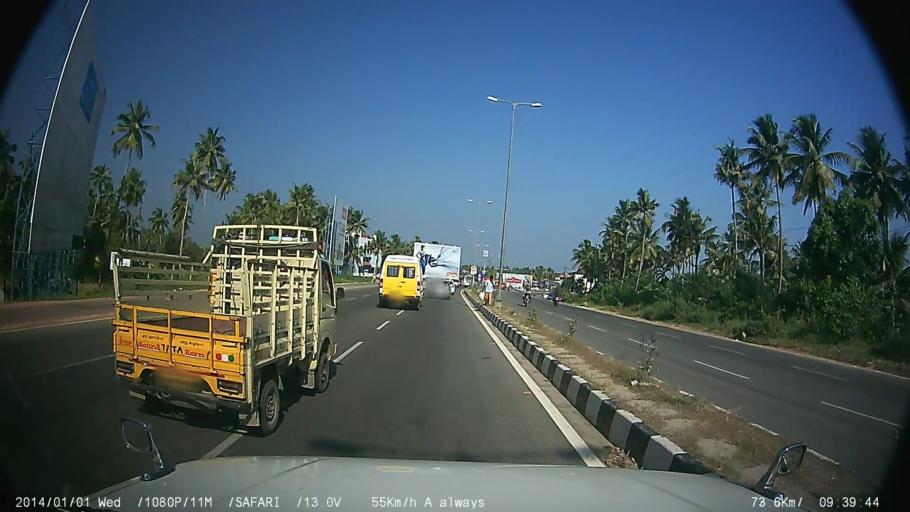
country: IN
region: Kerala
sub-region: Thrissur District
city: Irinjalakuda
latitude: 10.4242
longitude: 76.2688
